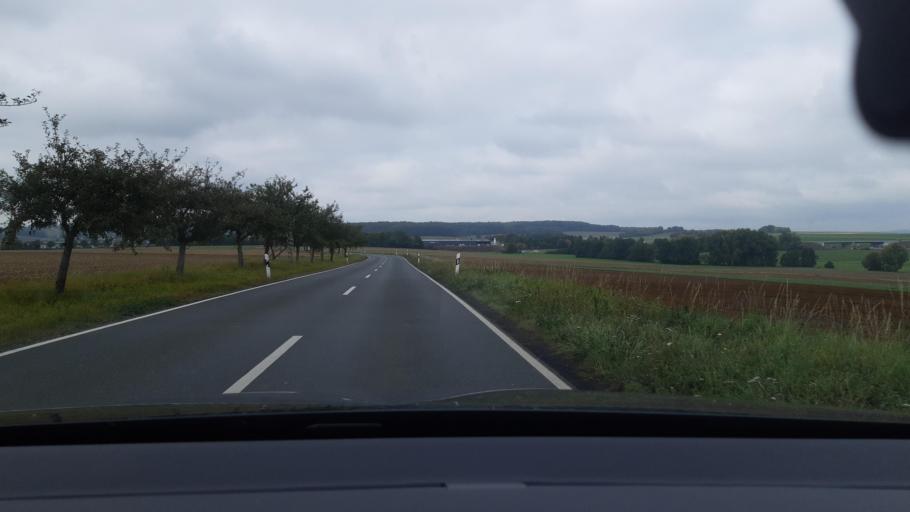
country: DE
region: Hesse
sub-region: Regierungsbezirk Giessen
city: Hoernsheim
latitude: 50.5215
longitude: 8.6045
